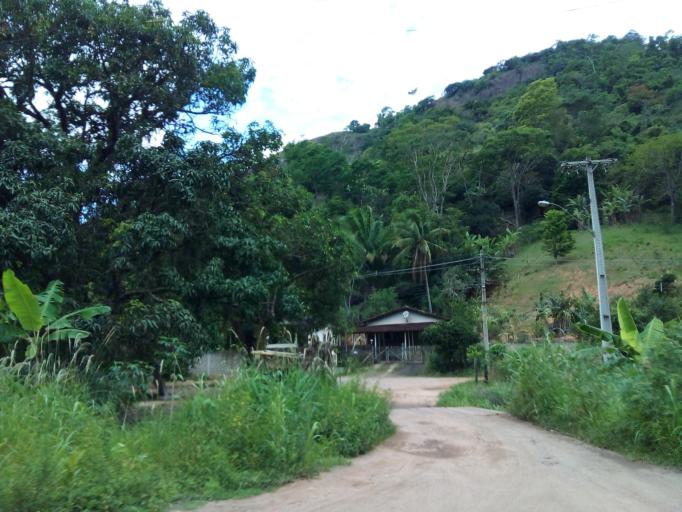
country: BR
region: Espirito Santo
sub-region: Joao Neiva
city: Joao Neiva
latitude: -19.7465
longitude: -40.3658
